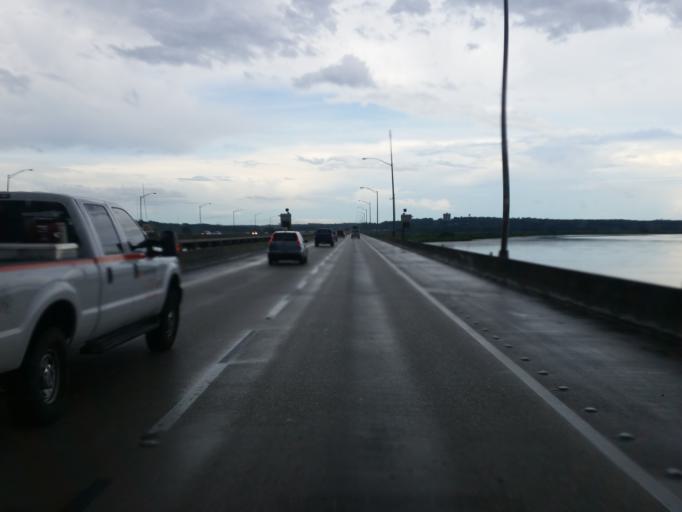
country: US
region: Alabama
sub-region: Baldwin County
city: Spanish Fort
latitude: 30.6591
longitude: -87.9415
